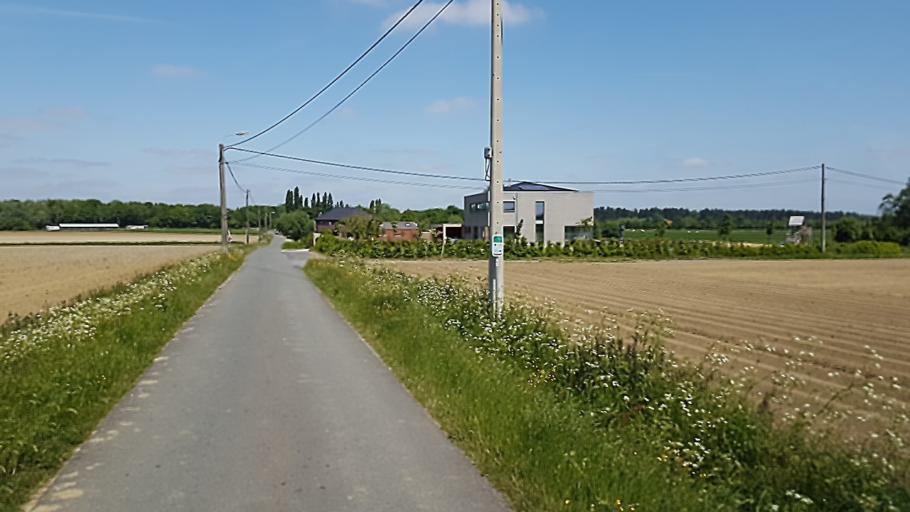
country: BE
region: Flanders
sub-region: Provincie West-Vlaanderen
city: Zonnebeke
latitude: 50.8431
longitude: 2.9773
